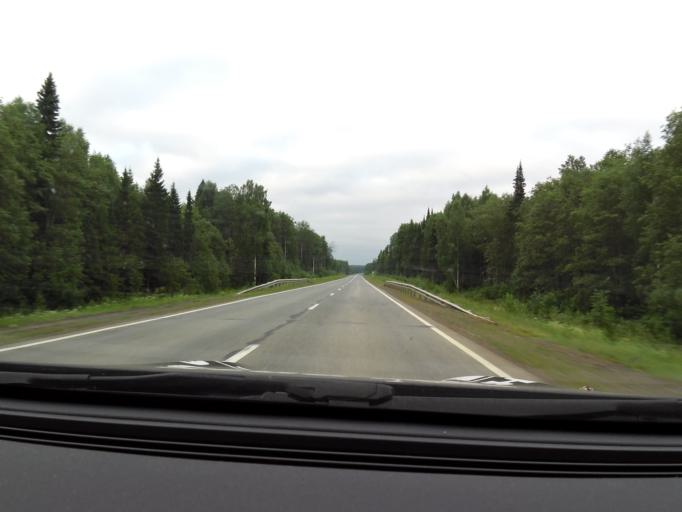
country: RU
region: Perm
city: Zyukayka
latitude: 58.3727
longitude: 54.6429
